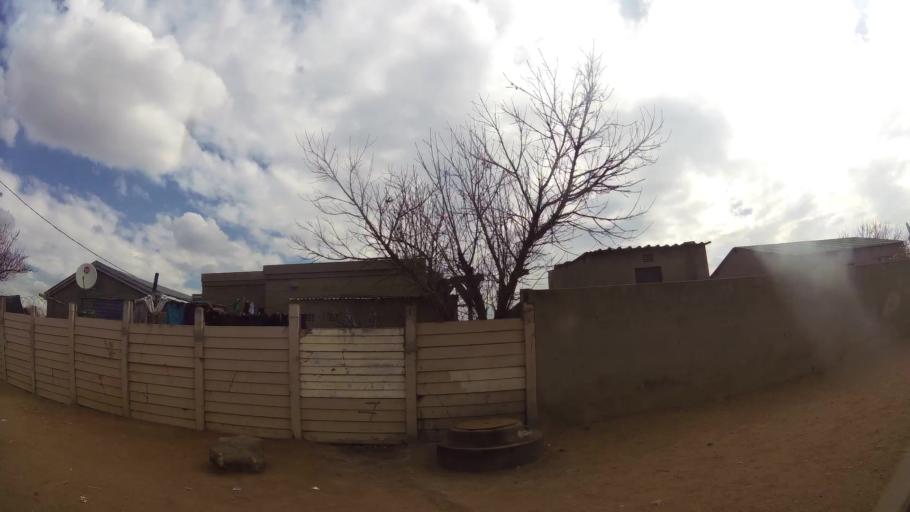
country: ZA
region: Gauteng
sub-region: Ekurhuleni Metropolitan Municipality
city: Germiston
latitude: -26.4031
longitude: 28.1681
